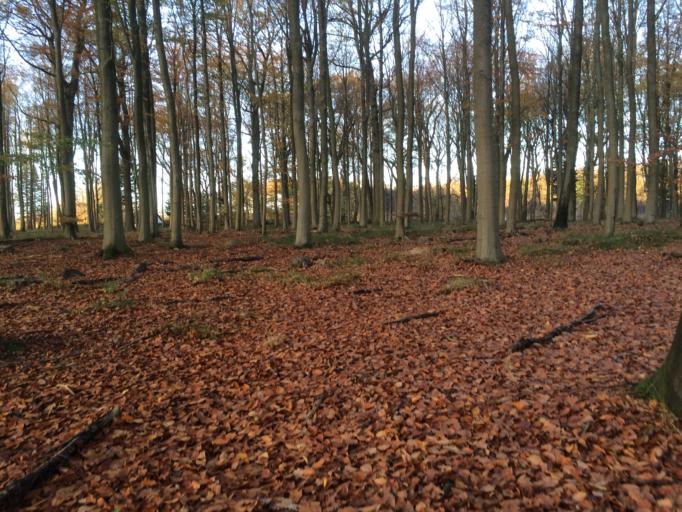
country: DK
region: Capital Region
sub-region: Fureso Kommune
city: Farum
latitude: 55.7932
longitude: 12.3473
